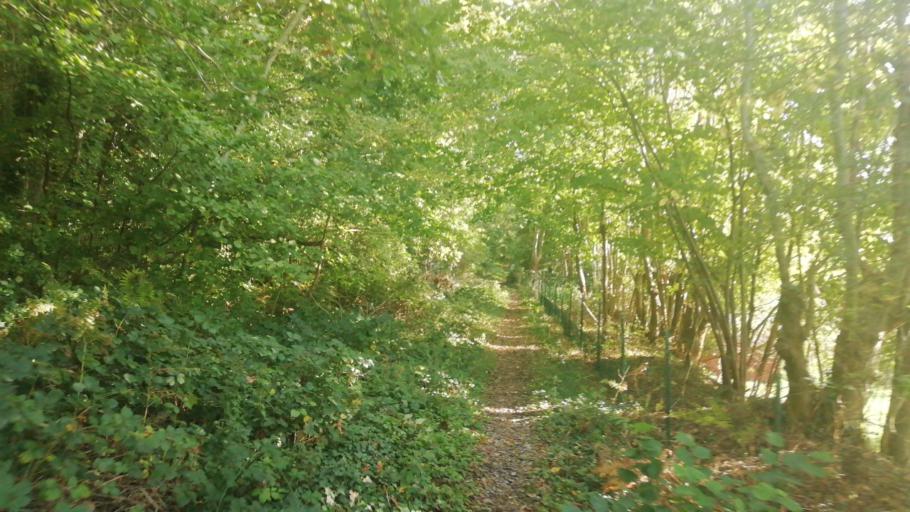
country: FR
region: Haute-Normandie
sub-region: Departement de la Seine-Maritime
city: Rolleville
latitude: 49.5874
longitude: 0.2129
